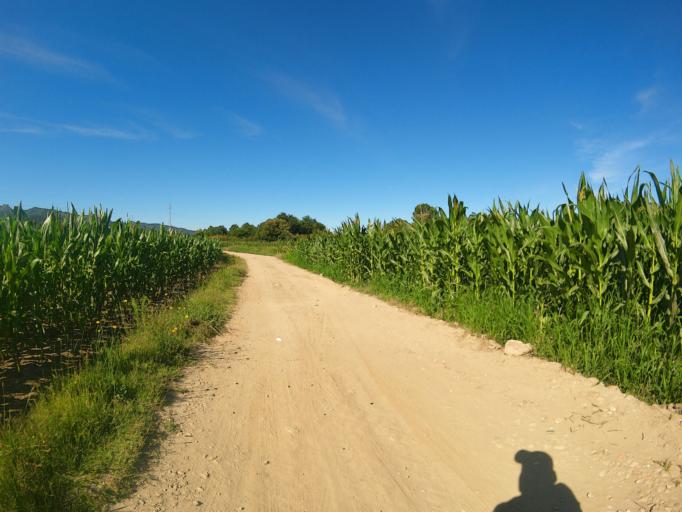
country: PT
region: Viana do Castelo
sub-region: Ponte de Lima
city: Ponte de Lima
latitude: 41.7418
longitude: -8.6418
